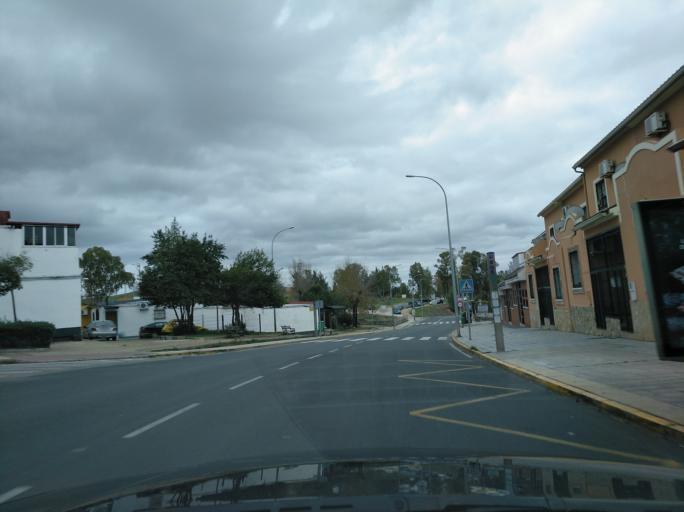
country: ES
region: Extremadura
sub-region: Provincia de Badajoz
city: Badajoz
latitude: 38.8902
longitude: -6.9766
